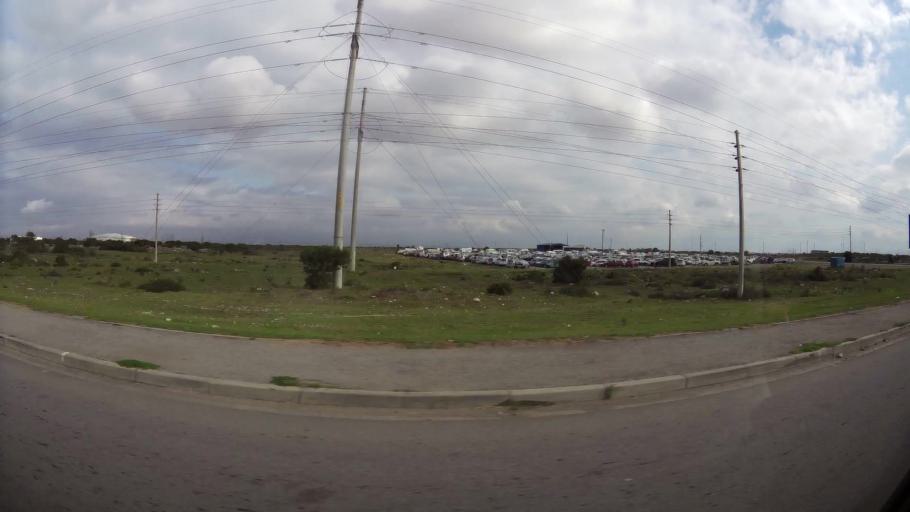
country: ZA
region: Eastern Cape
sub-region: Nelson Mandela Bay Metropolitan Municipality
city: Port Elizabeth
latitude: -33.8060
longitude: 25.6237
